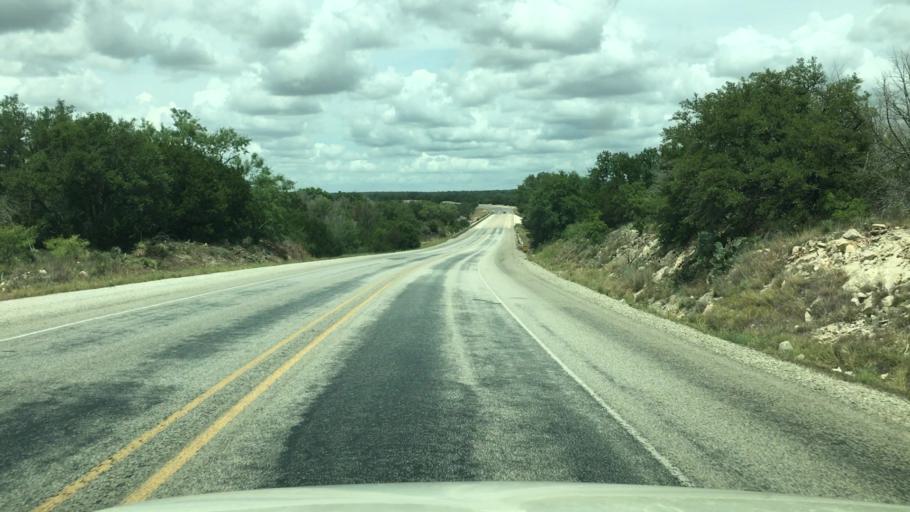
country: US
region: Texas
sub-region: McCulloch County
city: Brady
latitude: 31.0111
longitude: -99.2080
